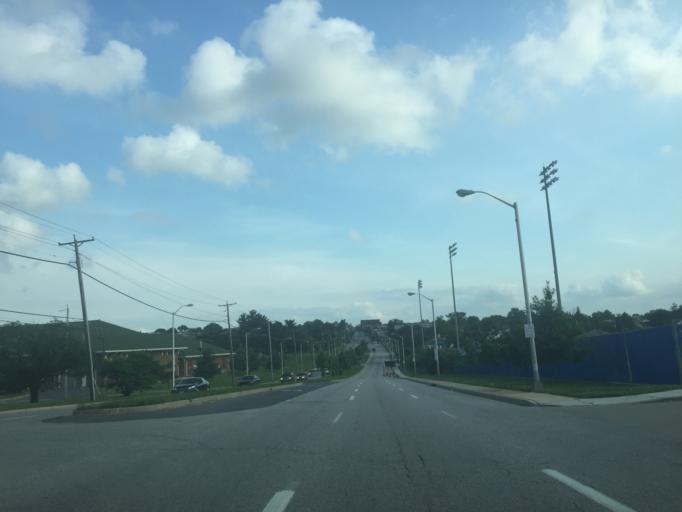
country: US
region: Maryland
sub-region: City of Baltimore
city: Baltimore
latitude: 39.3331
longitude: -76.5889
